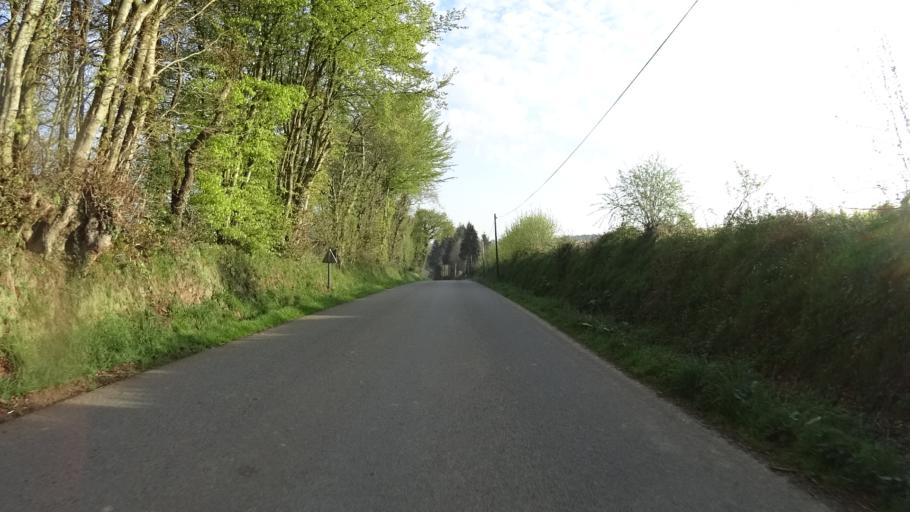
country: FR
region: Brittany
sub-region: Departement du Finistere
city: Sizun
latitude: 48.4296
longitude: -4.0719
